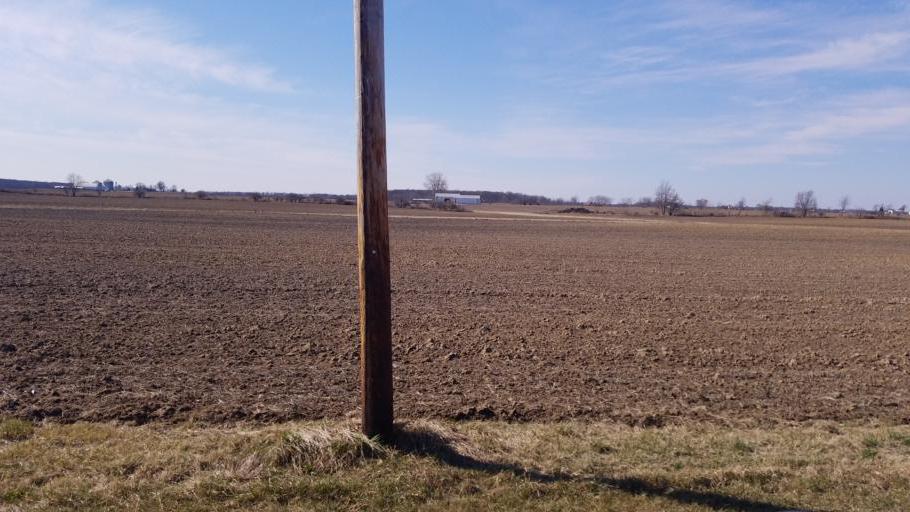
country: US
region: Ohio
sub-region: Hardin County
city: Kenton
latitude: 40.5335
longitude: -83.4557
